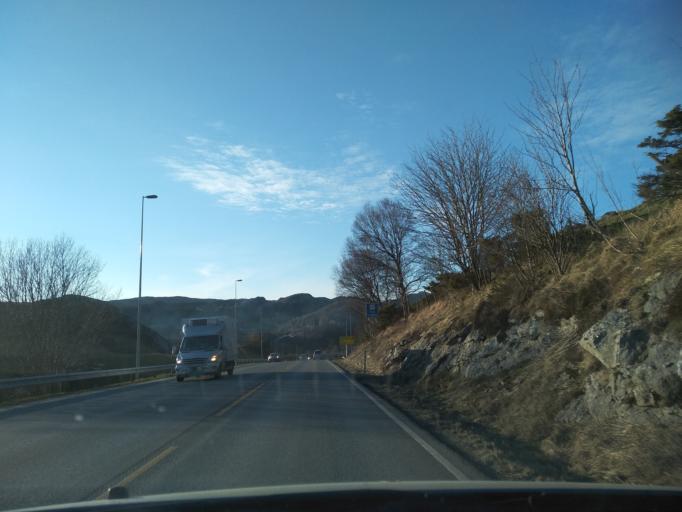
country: NO
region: Rogaland
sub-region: Tysvaer
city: Aksdal
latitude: 59.4621
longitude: 5.4793
